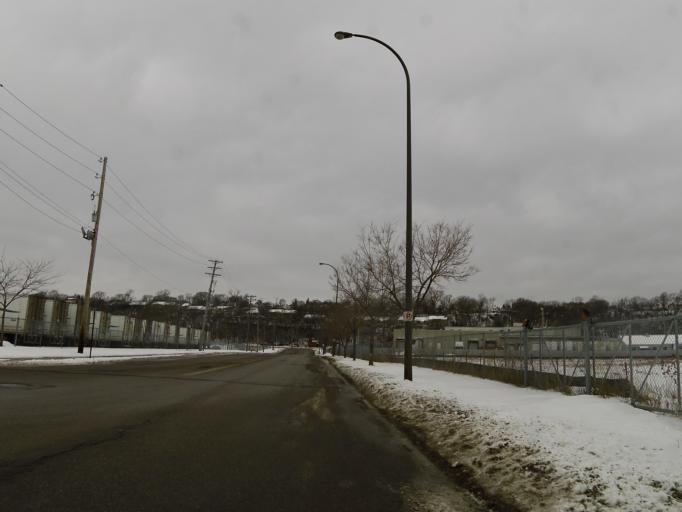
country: US
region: Minnesota
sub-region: Dakota County
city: South Saint Paul
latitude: 44.8858
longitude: -93.0293
